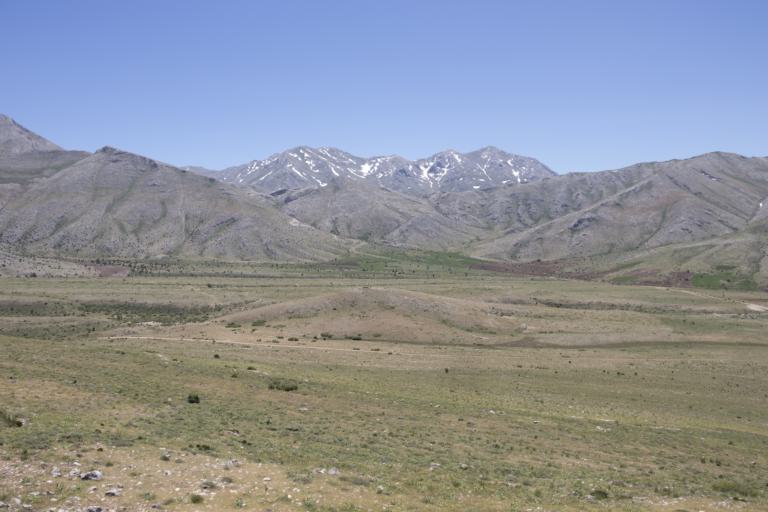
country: TR
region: Kayseri
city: Toklar
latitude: 38.4125
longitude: 36.1112
